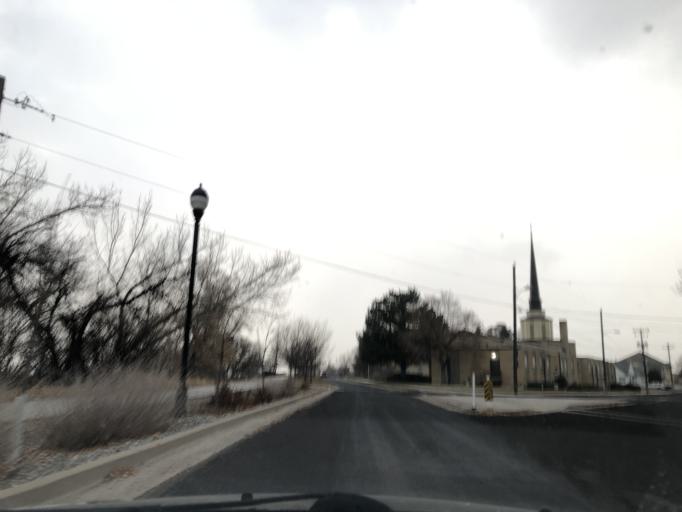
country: US
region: Utah
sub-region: Cache County
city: Logan
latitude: 41.7370
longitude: -111.8203
